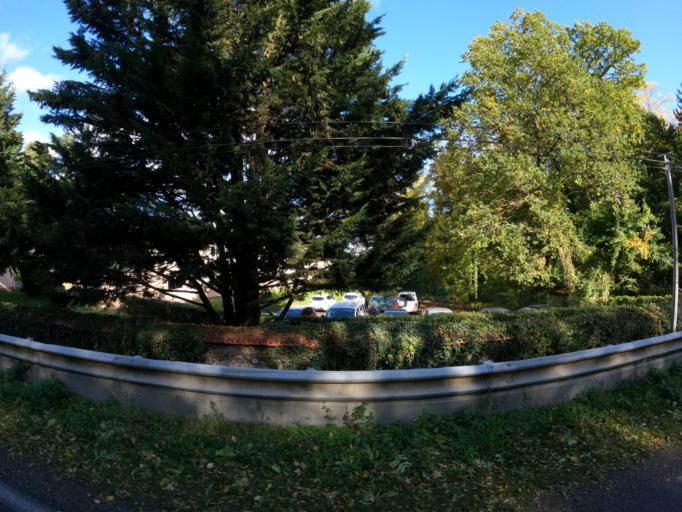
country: FR
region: Ile-de-France
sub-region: Departement de Seine-et-Marne
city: Montry
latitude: 48.8832
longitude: 2.8210
